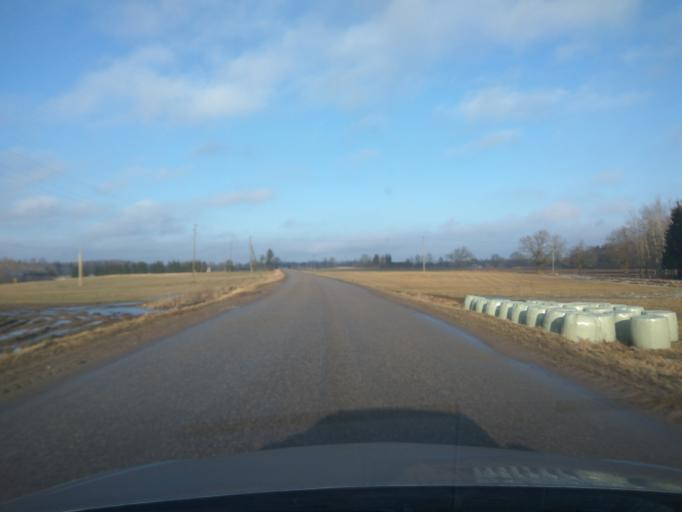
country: LV
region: Saldus Rajons
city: Saldus
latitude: 56.8364
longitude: 22.3784
